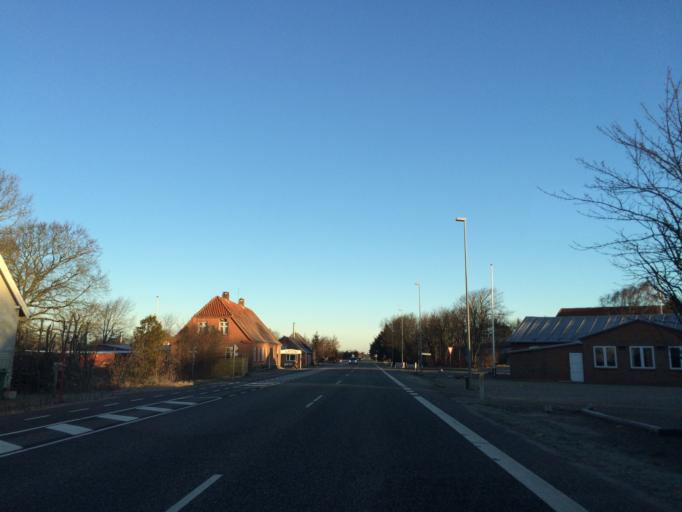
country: DK
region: Central Jutland
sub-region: Holstebro Kommune
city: Ulfborg
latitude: 56.3003
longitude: 8.3388
